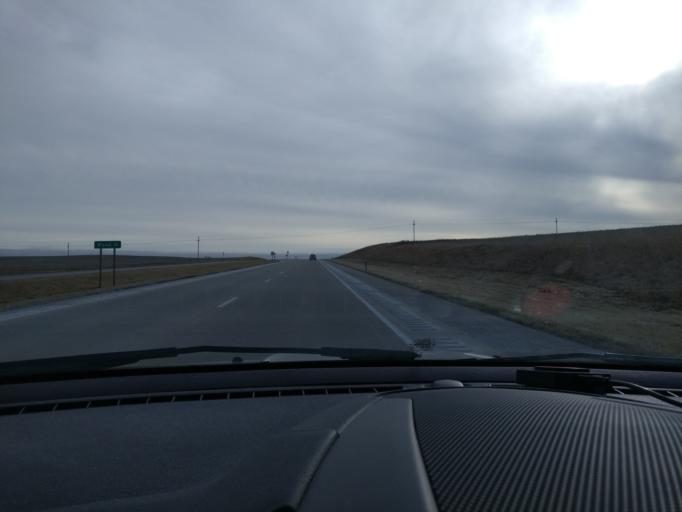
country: US
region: Nebraska
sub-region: Saunders County
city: Wahoo
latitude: 41.1641
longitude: -96.6314
